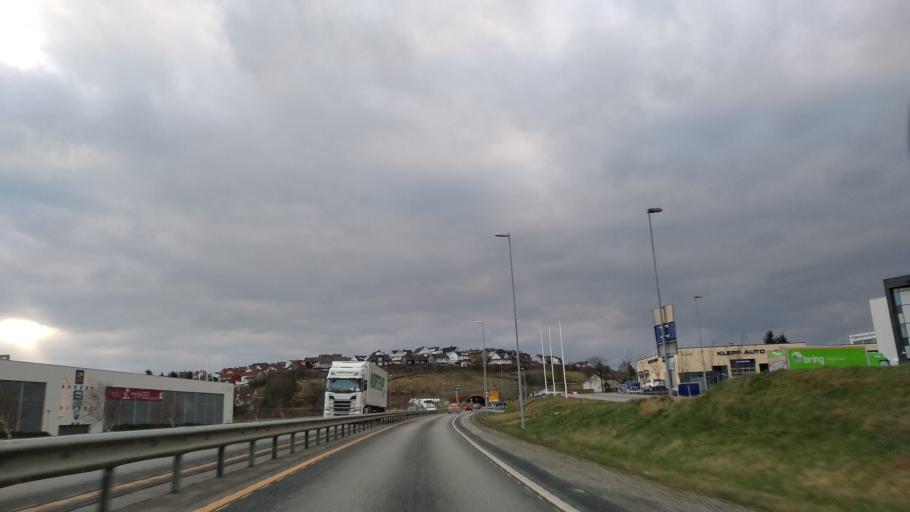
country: NO
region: Rogaland
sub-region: Klepp
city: Kleppe
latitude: 58.7807
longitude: 5.6257
